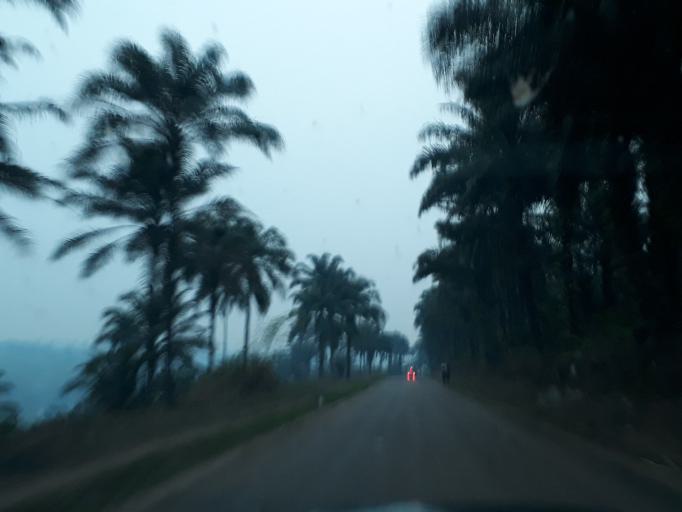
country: CD
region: Bandundu
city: Kikwit
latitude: -5.0690
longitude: 18.8683
